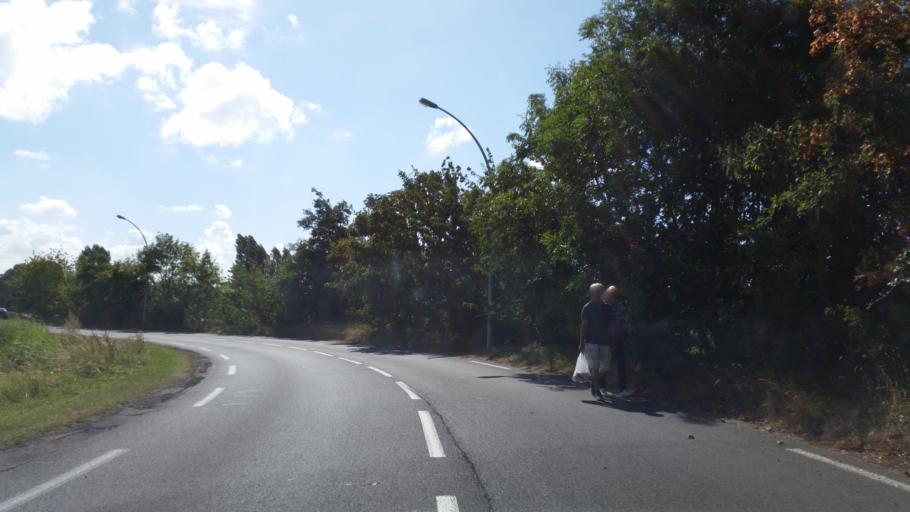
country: FR
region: Lower Normandy
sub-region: Departement du Calvados
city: Ouistreham
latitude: 49.2723
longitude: -0.2527
